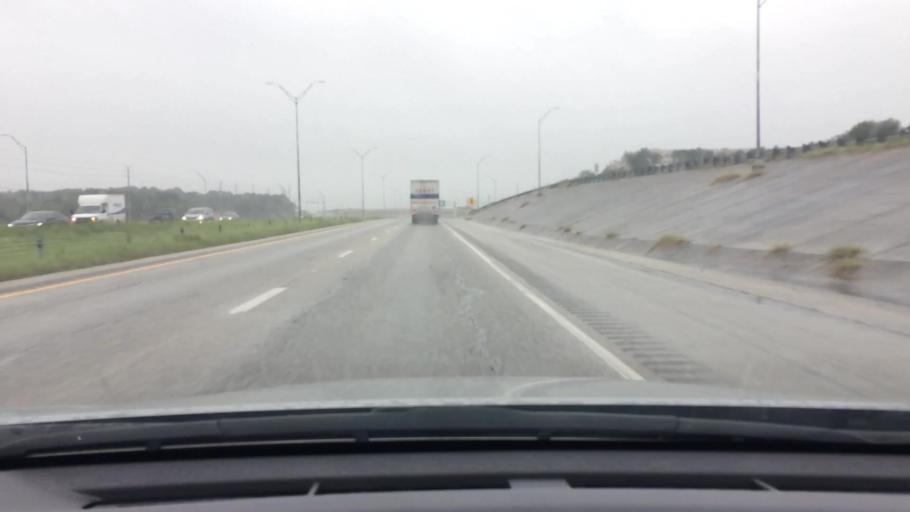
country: US
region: Texas
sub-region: Bexar County
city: Leon Valley
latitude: 29.4706
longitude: -98.6957
